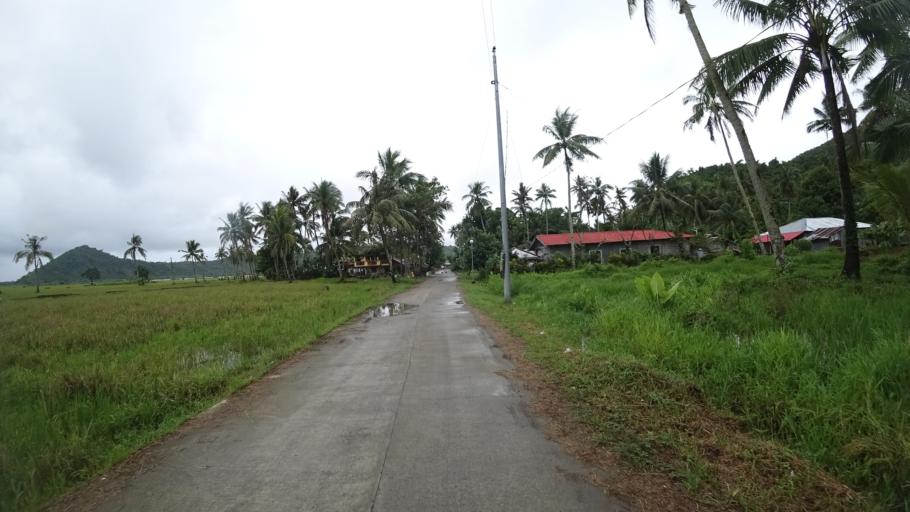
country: PH
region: Eastern Visayas
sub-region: Province of Leyte
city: Bugho
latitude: 10.7991
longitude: 124.9711
